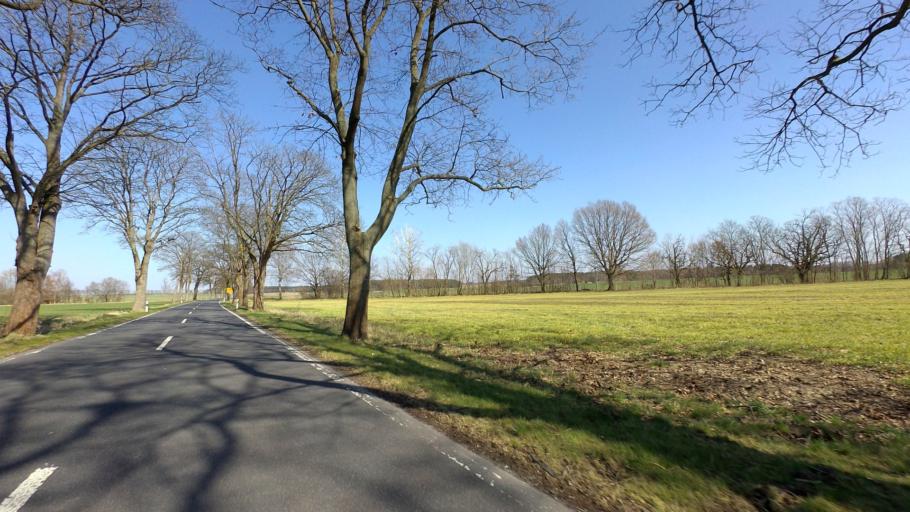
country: DE
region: Brandenburg
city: Sonnenberg
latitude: 52.9858
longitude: 13.0473
